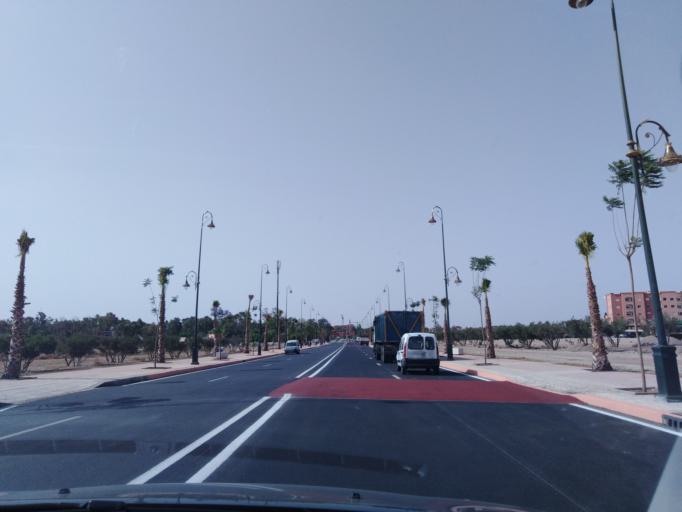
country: MA
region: Marrakech-Tensift-Al Haouz
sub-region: Kelaa-Des-Sraghna
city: Sidi Bou Othmane
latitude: 32.2263
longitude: -7.9570
